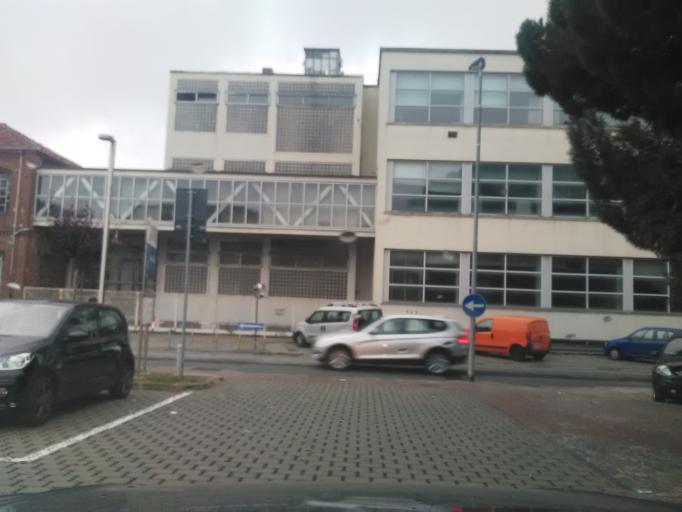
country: IT
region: Piedmont
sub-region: Provincia di Torino
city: Ivrea
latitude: 45.4601
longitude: 7.8751
